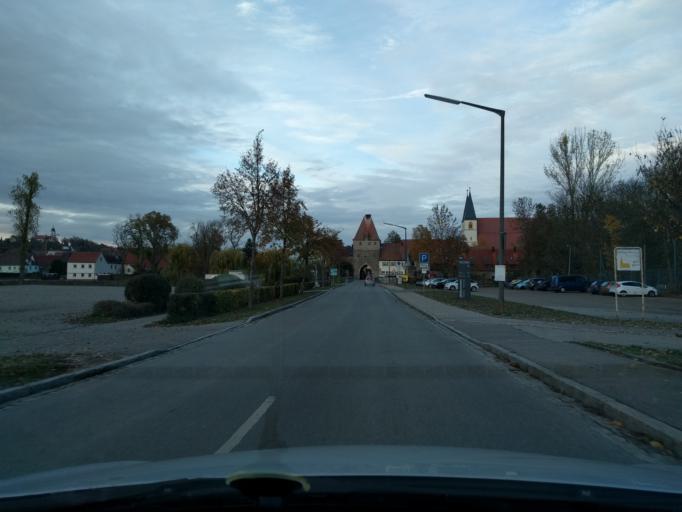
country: DE
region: Bavaria
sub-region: Regierungsbezirk Mittelfranken
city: Herrieden
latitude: 49.2308
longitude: 10.4961
